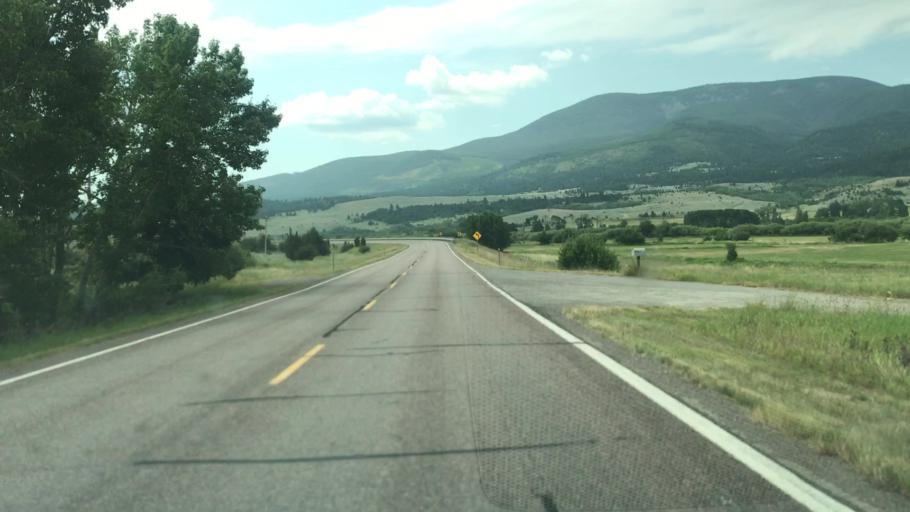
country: US
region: Montana
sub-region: Lewis and Clark County
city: Lincoln
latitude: 46.8395
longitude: -112.8992
